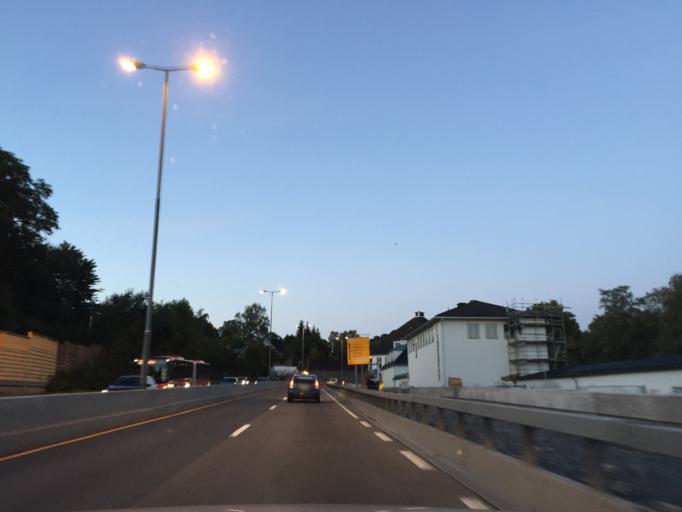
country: NO
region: Oslo
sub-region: Oslo
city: Sjolyststranda
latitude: 59.9451
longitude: 10.7047
